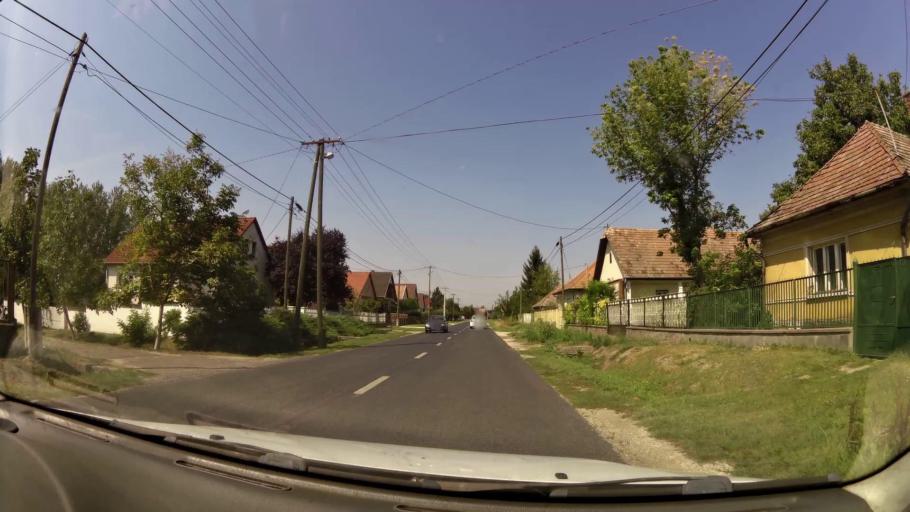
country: HU
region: Pest
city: Tapiobicske
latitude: 47.3665
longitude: 19.6862
